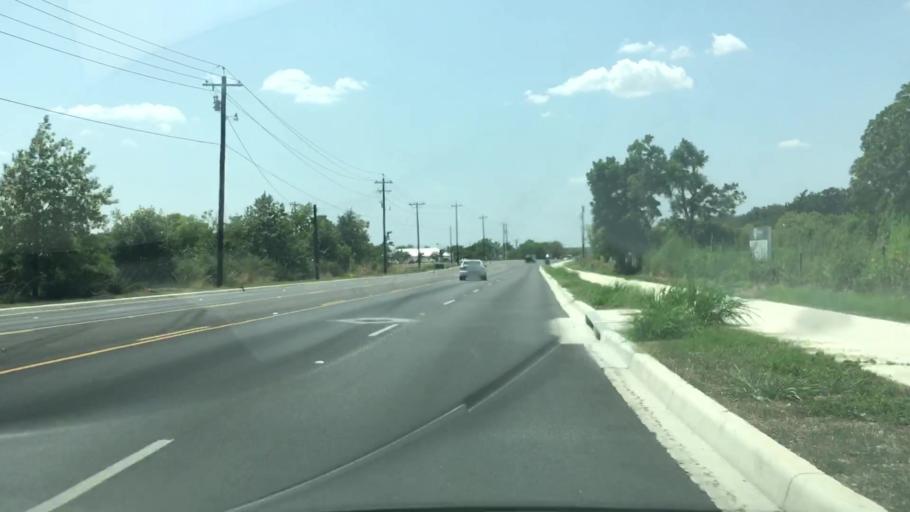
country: US
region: Texas
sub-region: Guadalupe County
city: Cibolo
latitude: 29.5699
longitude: -98.2423
